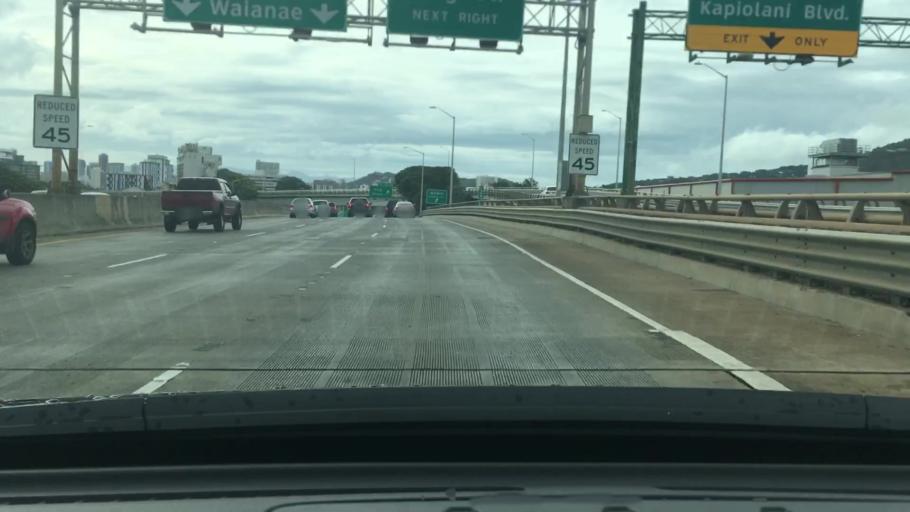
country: US
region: Hawaii
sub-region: Honolulu County
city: Honolulu
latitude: 21.2884
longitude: -157.8135
